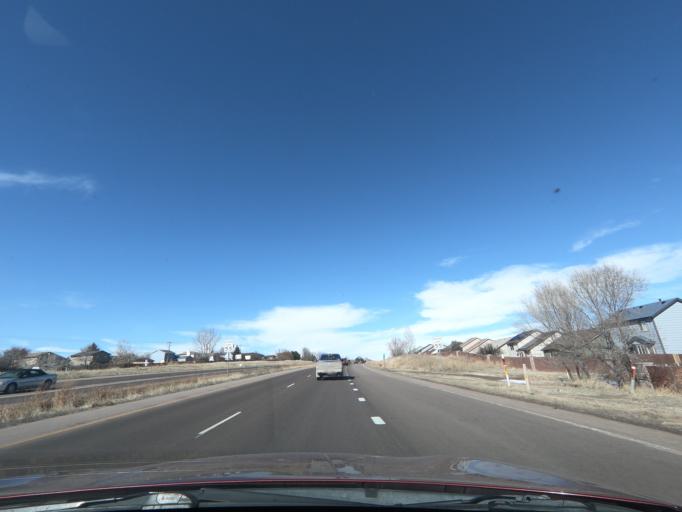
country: US
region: Colorado
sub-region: El Paso County
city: Security-Widefield
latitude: 38.7235
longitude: -104.6821
